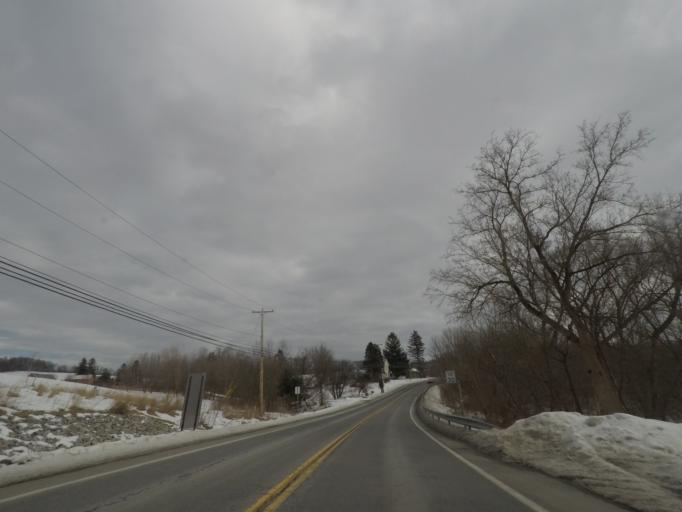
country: US
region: New York
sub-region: Washington County
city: Greenwich
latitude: 43.0845
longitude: -73.4897
